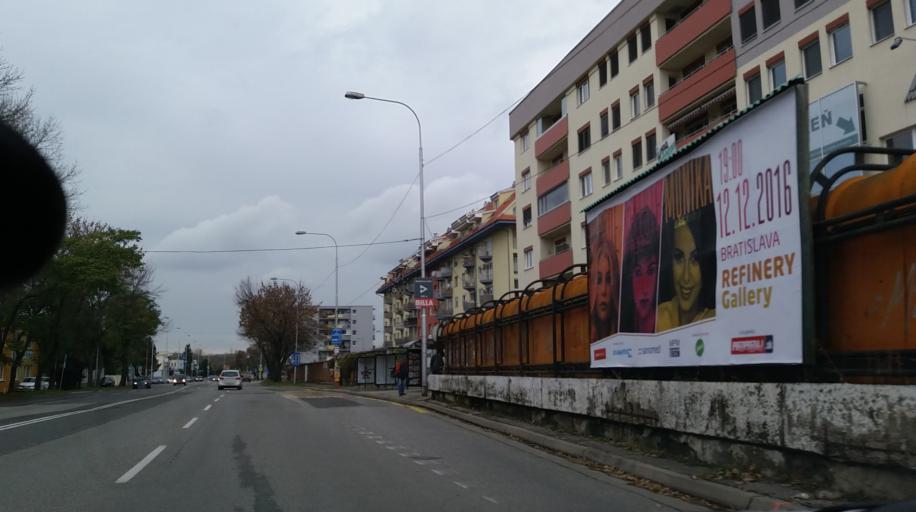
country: SK
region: Bratislavsky
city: Bratislava
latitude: 48.1259
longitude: 17.0964
